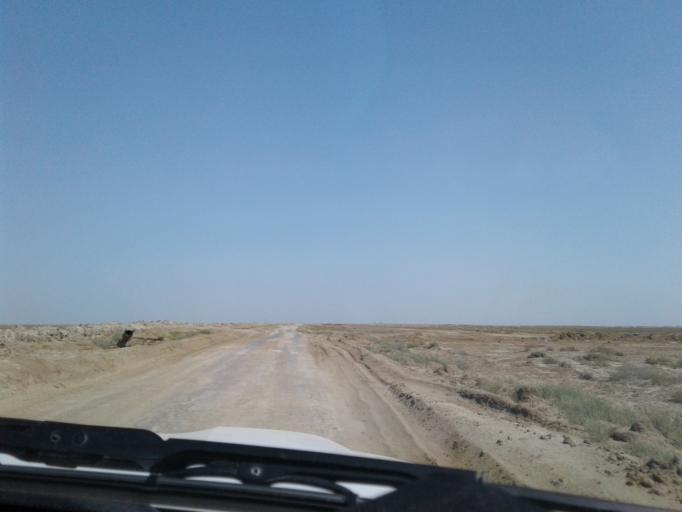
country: IR
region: Golestan
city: Gomishan
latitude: 37.8266
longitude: 53.9215
